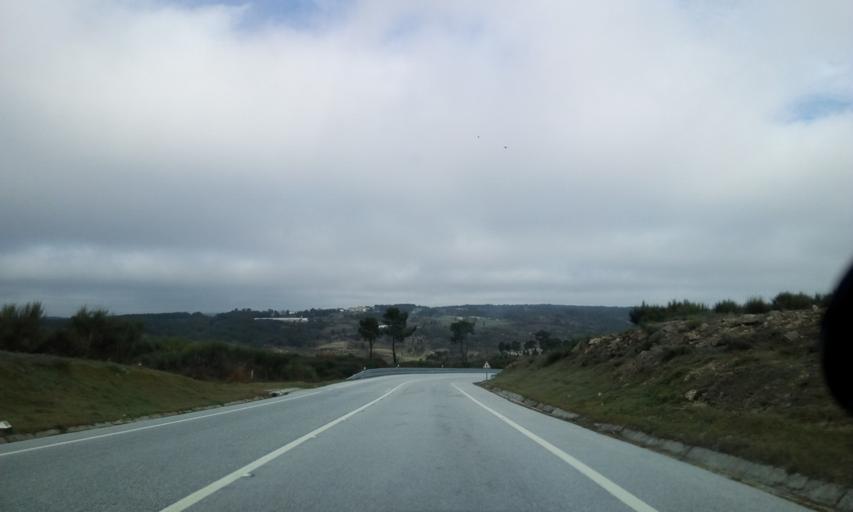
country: PT
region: Guarda
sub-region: Aguiar da Beira
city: Aguiar da Beira
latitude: 40.7715
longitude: -7.5039
